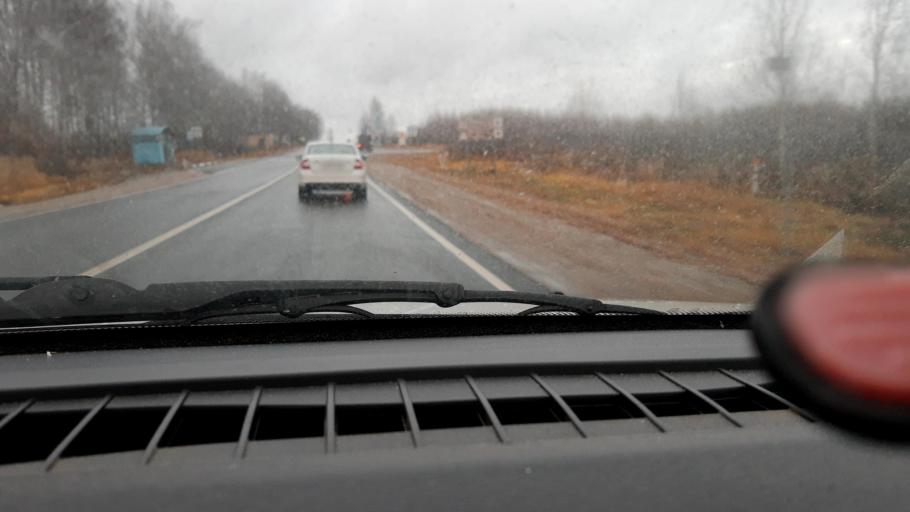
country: RU
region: Nizjnij Novgorod
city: Krasnyye Baki
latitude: 57.0934
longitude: 45.1499
